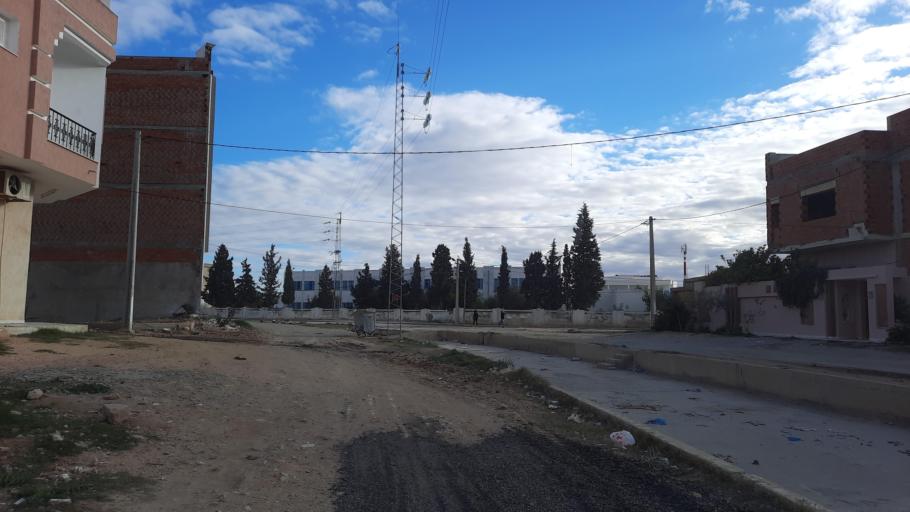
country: TN
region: Al Mahdiyah
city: El Jem
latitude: 35.2867
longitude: 10.7040
